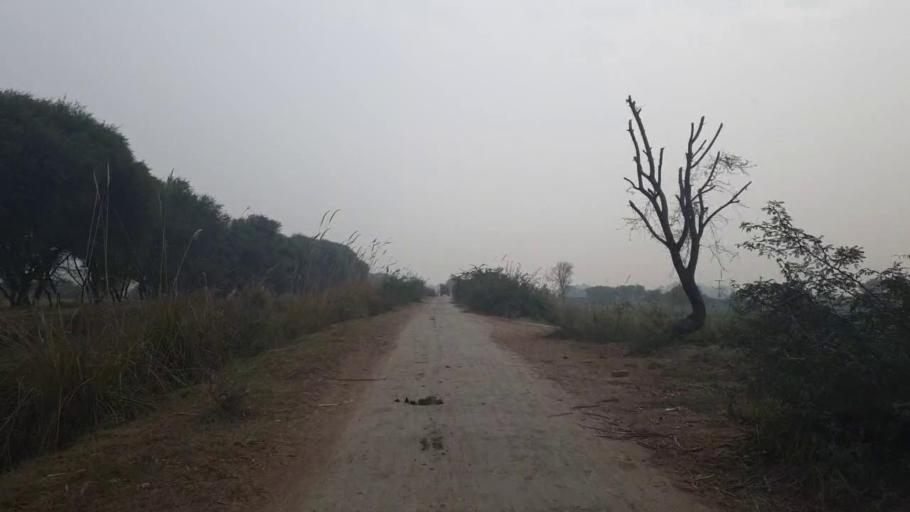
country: PK
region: Sindh
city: Tando Adam
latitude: 25.7518
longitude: 68.7004
